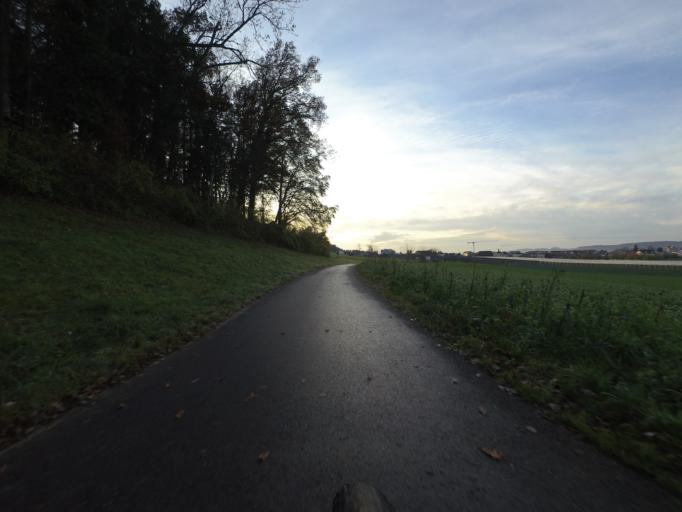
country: CH
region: Thurgau
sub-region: Frauenfeld District
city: Pfyn
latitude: 47.5733
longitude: 8.9541
